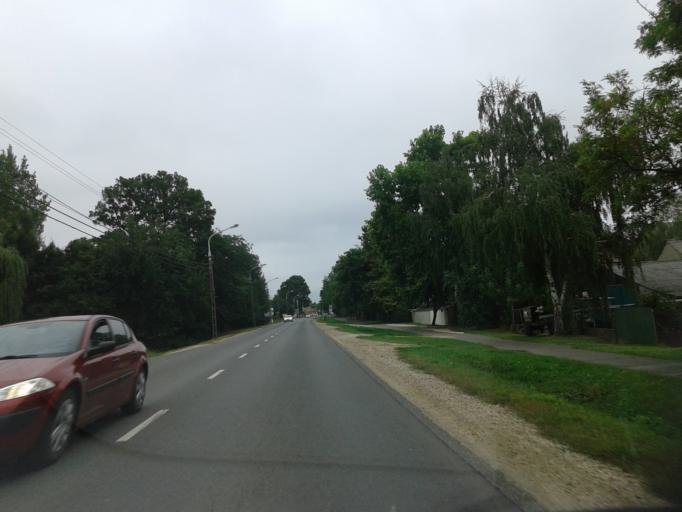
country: HU
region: Bacs-Kiskun
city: Solt
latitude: 46.8000
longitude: 19.0248
